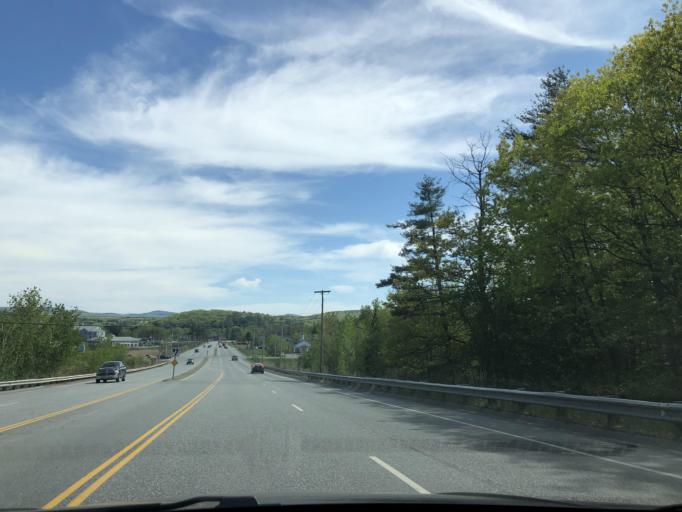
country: US
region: New Hampshire
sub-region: Grafton County
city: Lebanon
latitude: 43.6611
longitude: -72.2460
